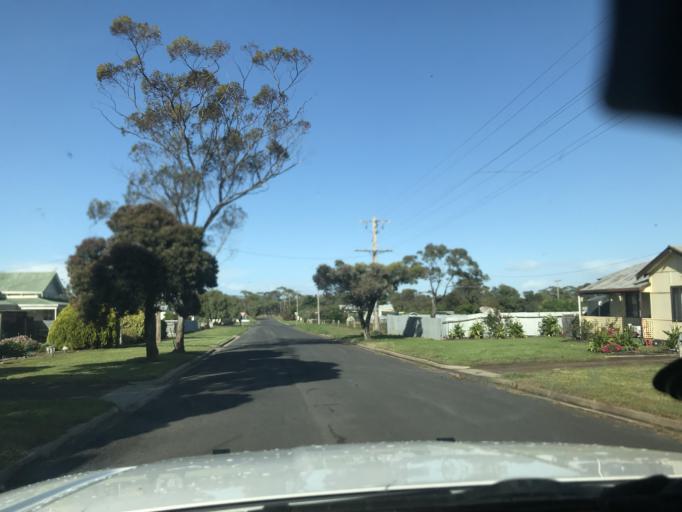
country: AU
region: Victoria
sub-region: Horsham
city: Horsham
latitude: -36.7206
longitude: 141.4747
